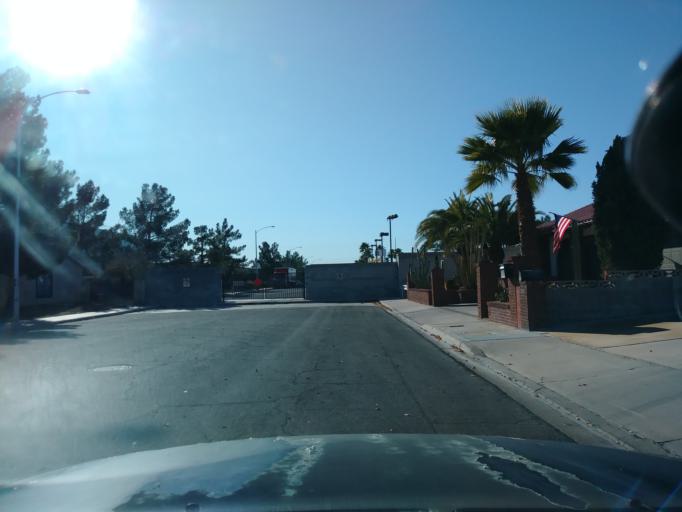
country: US
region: Nevada
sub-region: Clark County
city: Spring Valley
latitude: 36.1465
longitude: -115.2298
